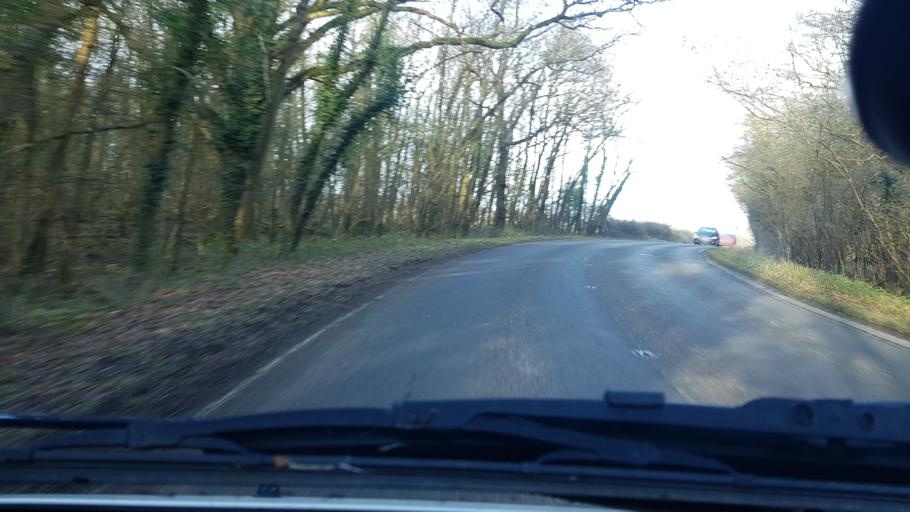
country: GB
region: England
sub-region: Surrey
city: Normandy
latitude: 51.2347
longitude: -0.6707
